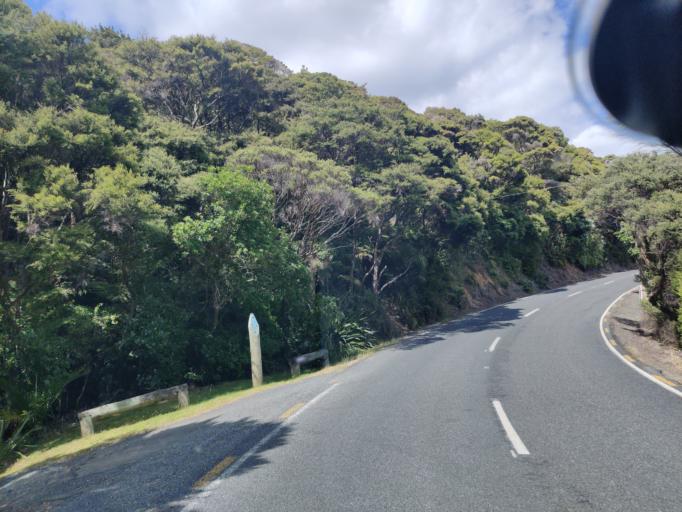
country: NZ
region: Northland
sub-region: Far North District
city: Paihia
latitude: -35.2583
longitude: 174.2336
